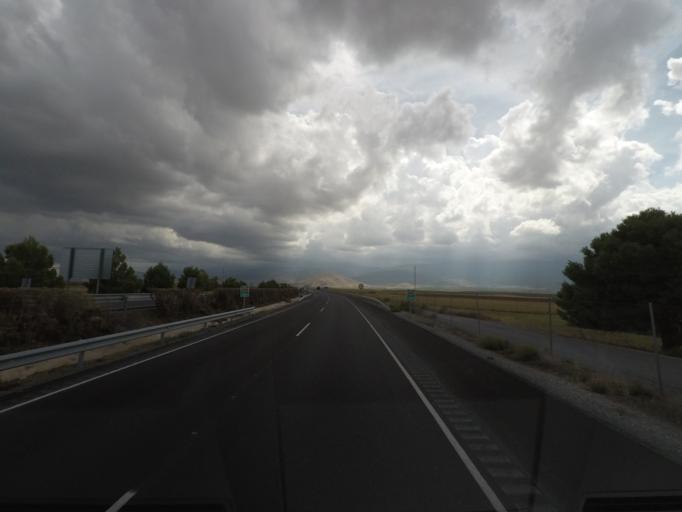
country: ES
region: Andalusia
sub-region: Provincia de Granada
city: Albunan
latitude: 37.2263
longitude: -3.0812
